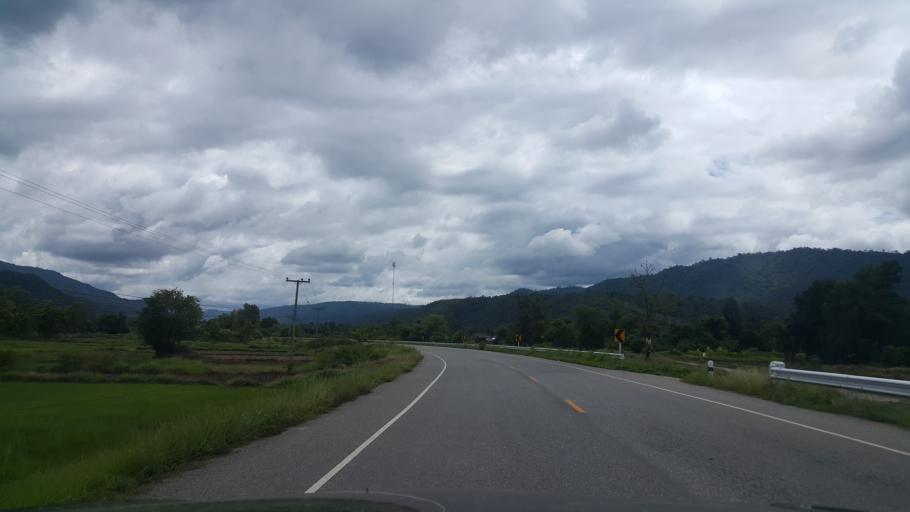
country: TH
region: Phitsanulok
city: Chat Trakan
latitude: 17.3005
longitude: 100.6638
